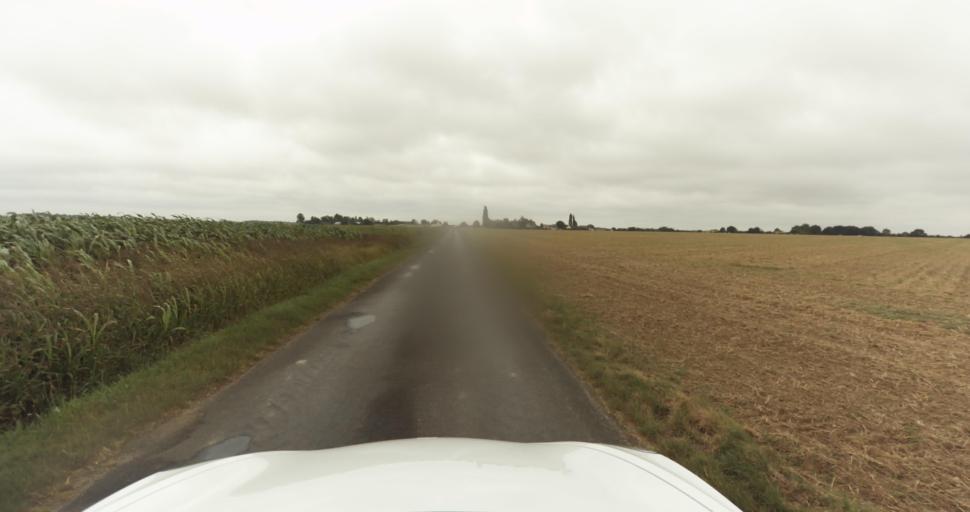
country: FR
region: Haute-Normandie
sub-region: Departement de l'Eure
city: Aviron
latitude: 49.0751
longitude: 1.0711
